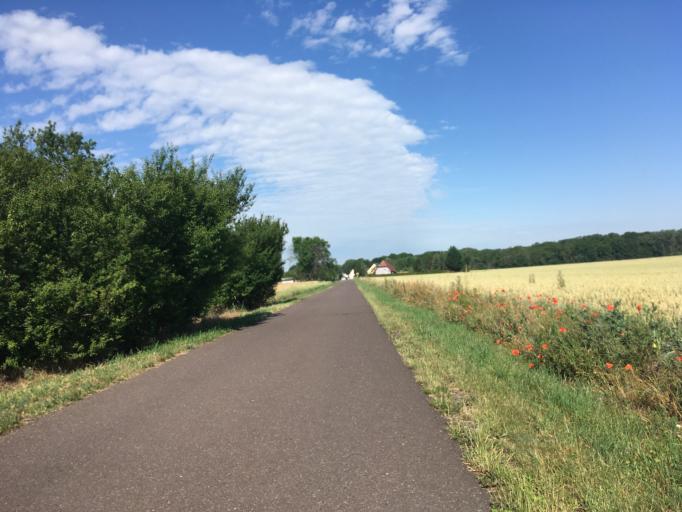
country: DE
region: Saxony-Anhalt
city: Wulfen
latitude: 51.7729
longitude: 11.9218
